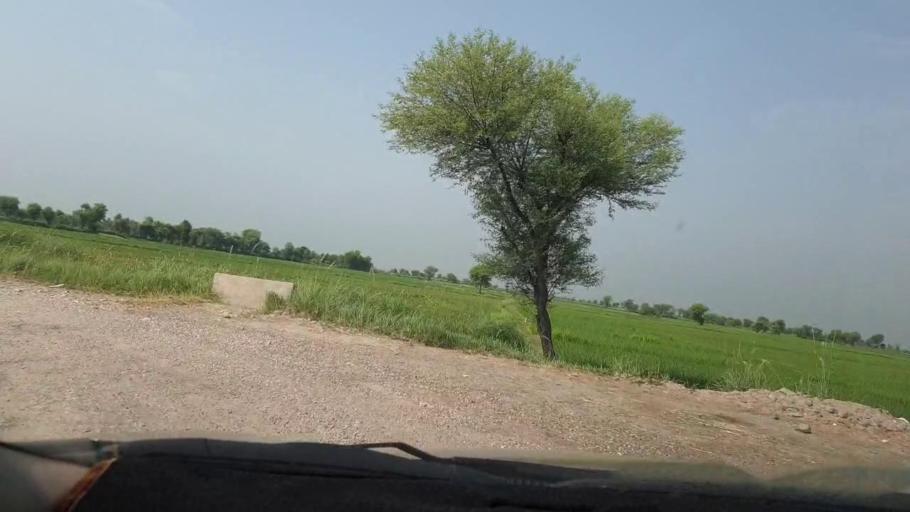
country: PK
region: Sindh
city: Goth Garelo
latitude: 27.4437
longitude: 68.0374
